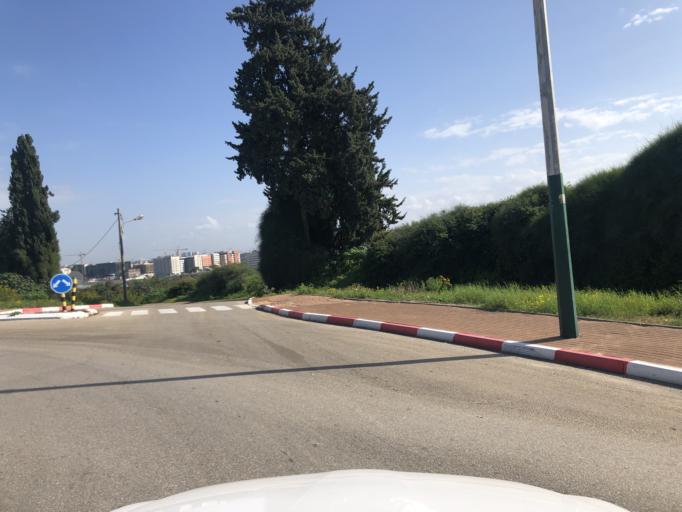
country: IL
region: Central District
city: Ness Ziona
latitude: 31.9140
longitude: 34.7932
